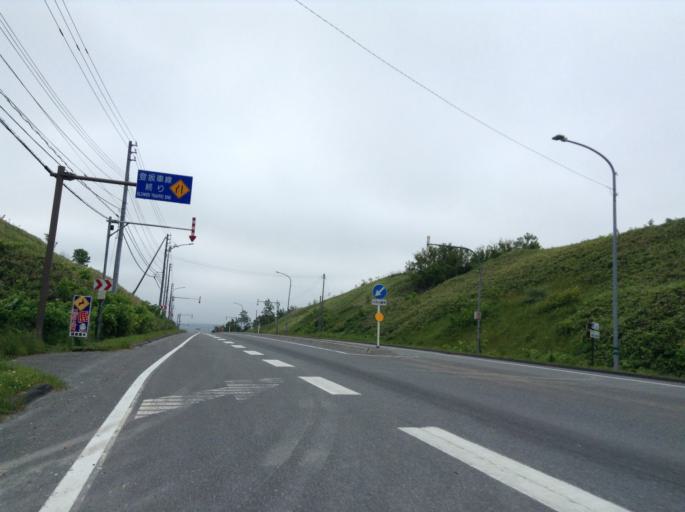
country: JP
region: Hokkaido
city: Wakkanai
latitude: 45.3740
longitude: 141.7159
